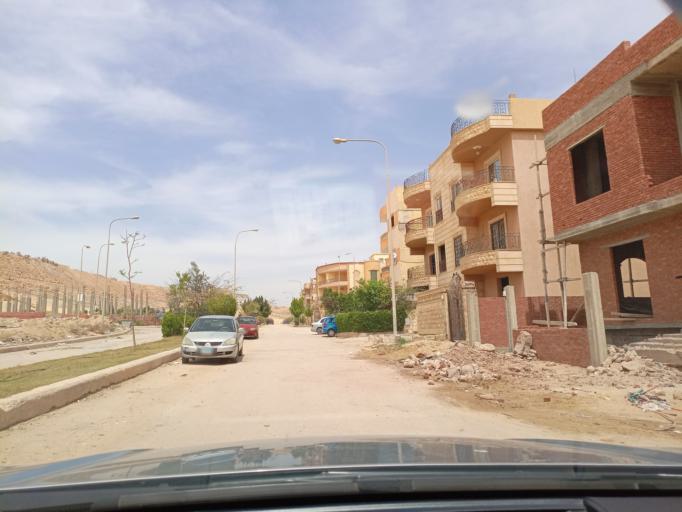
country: EG
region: Muhafazat al Qalyubiyah
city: Al Khankah
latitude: 30.2381
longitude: 31.4865
